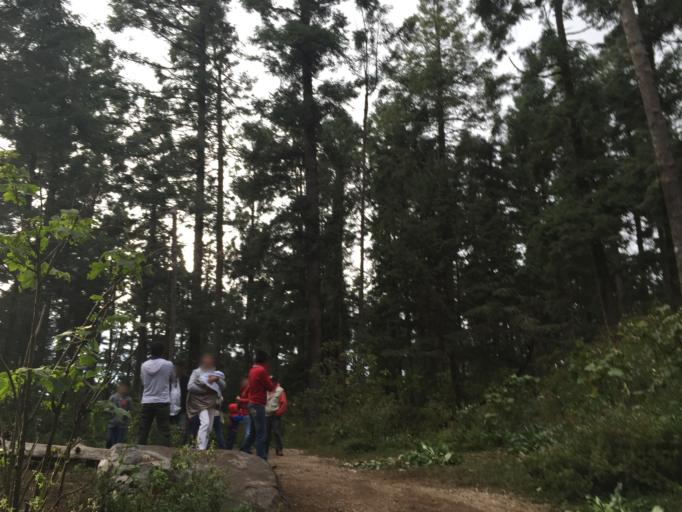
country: MX
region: Michoacan
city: Mineral de Angangueo
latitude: 19.6730
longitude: -100.2929
